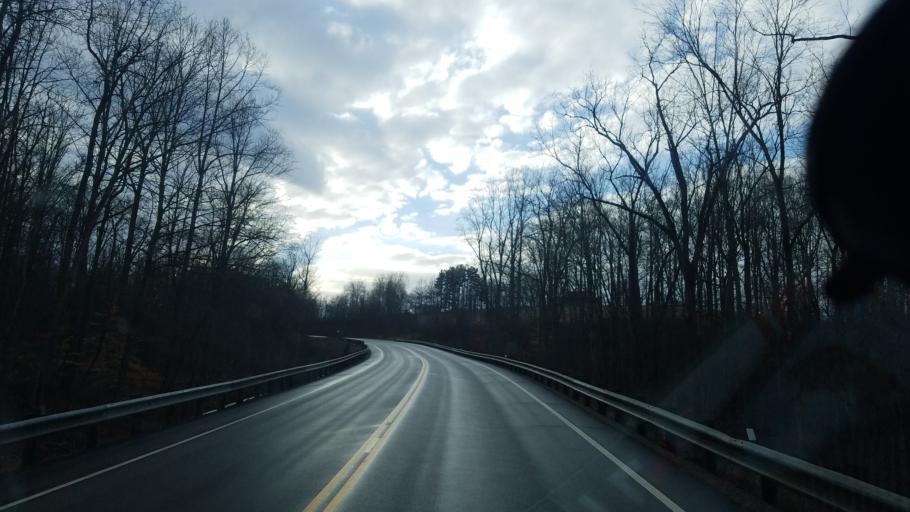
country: US
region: Ohio
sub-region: Knox County
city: Oak Hill
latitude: 40.3420
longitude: -82.1042
